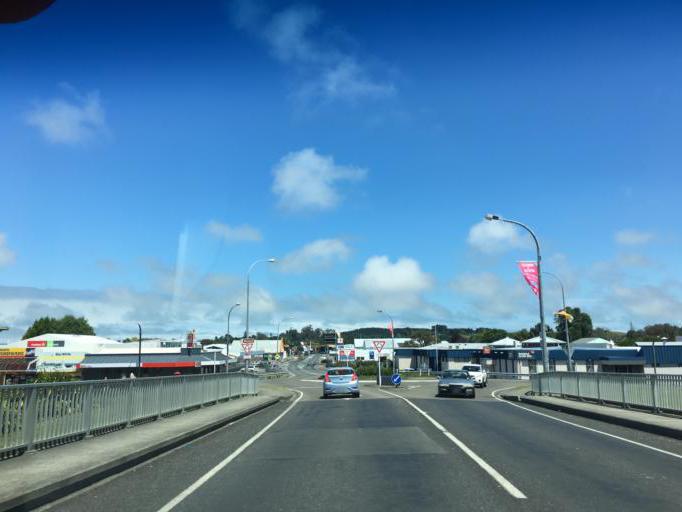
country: NZ
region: Hawke's Bay
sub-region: Wairoa District
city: Wairoa
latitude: -39.0324
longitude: 177.4185
